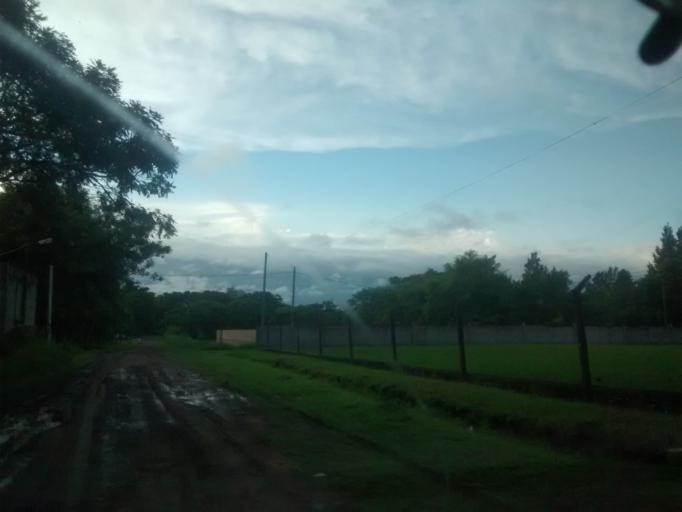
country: AR
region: Chaco
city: Fontana
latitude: -27.4190
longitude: -59.0043
